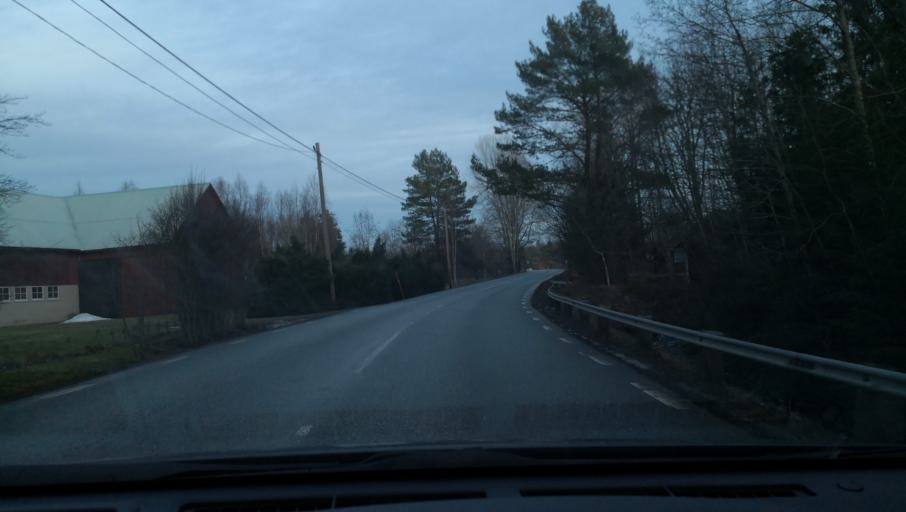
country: SE
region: OErebro
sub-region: Degerfors Kommun
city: Degerfors
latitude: 59.1344
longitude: 14.4121
